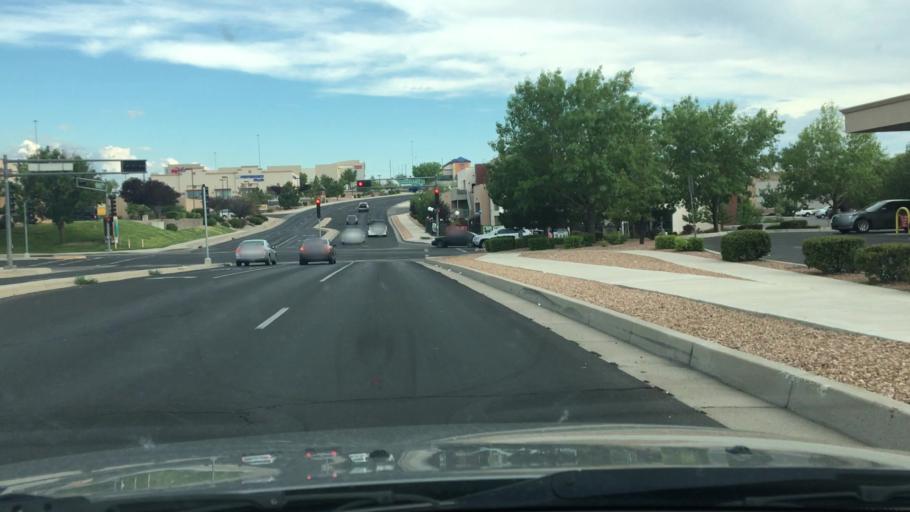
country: US
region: New Mexico
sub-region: Bernalillo County
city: North Valley
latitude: 35.1381
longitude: -106.6108
